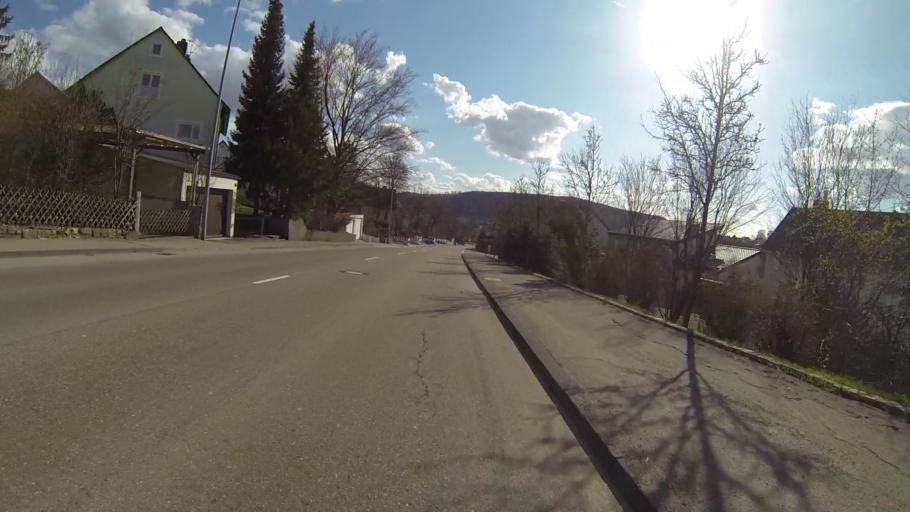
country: DE
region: Baden-Wuerttemberg
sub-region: Regierungsbezirk Stuttgart
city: Heidenheim an der Brenz
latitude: 48.6840
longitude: 10.1411
